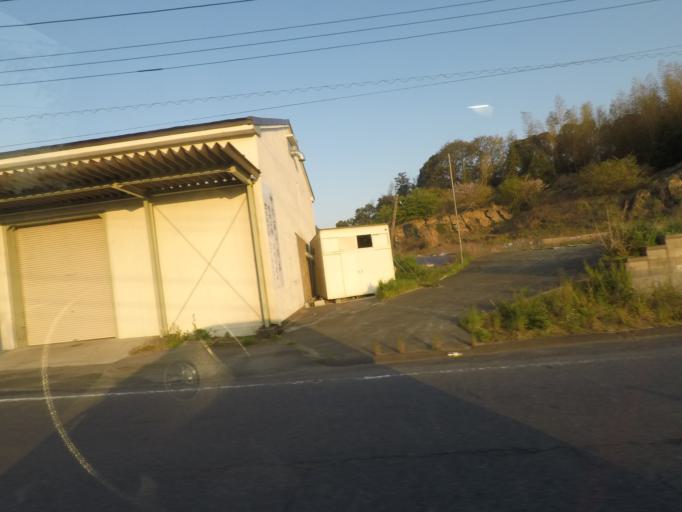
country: JP
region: Chiba
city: Narita
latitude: 35.7904
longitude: 140.3366
